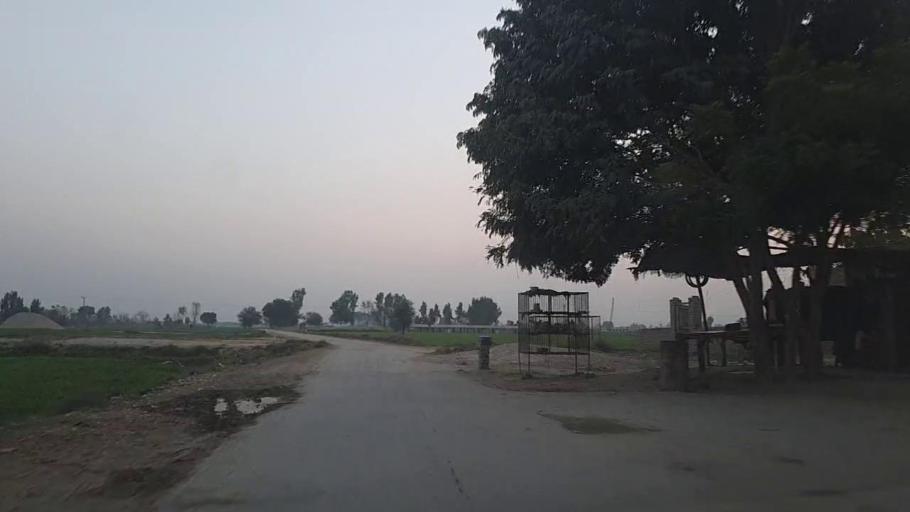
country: PK
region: Sindh
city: Naushahro Firoz
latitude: 26.8671
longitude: 68.0472
